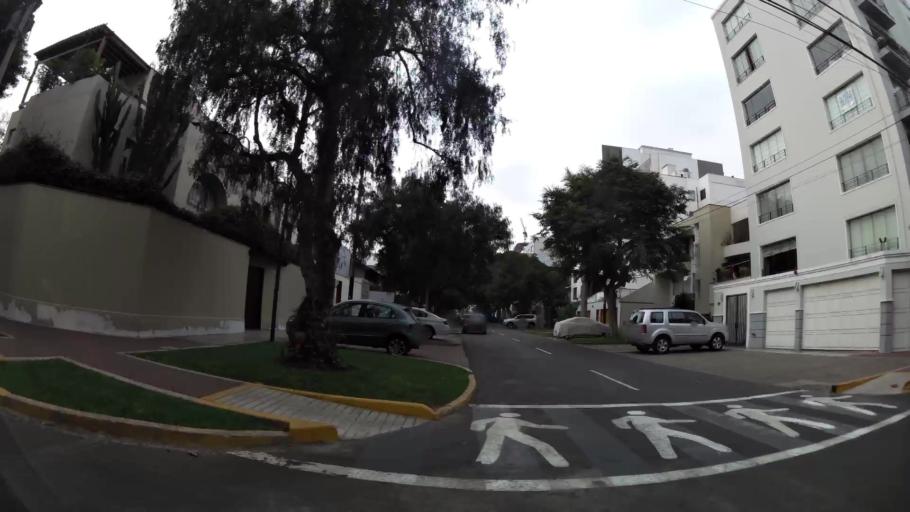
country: PE
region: Lima
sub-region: Lima
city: San Isidro
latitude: -12.1059
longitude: -77.0459
